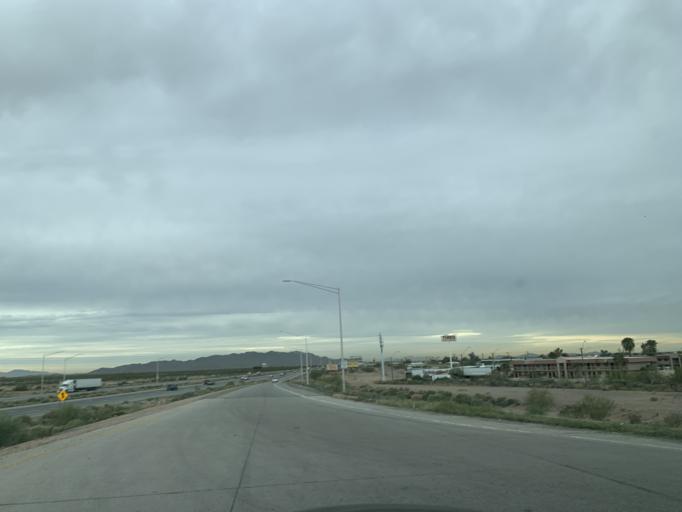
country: US
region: Arizona
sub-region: Pinal County
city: Arizona City
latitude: 32.7780
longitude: -111.6197
